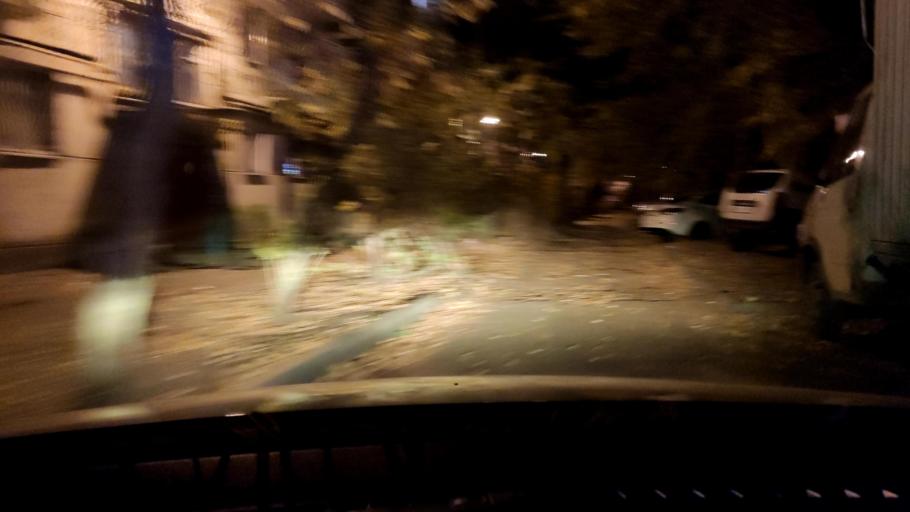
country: RU
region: Voronezj
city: Voronezh
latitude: 51.6476
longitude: 39.1418
